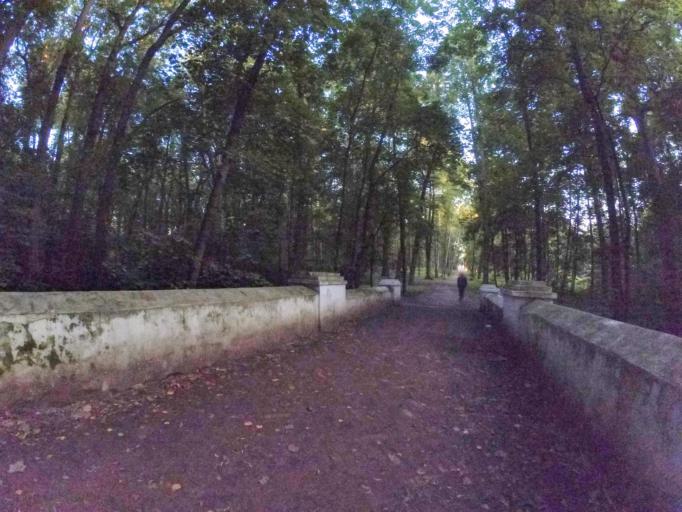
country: RU
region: Moscow
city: Strogino
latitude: 55.8505
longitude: 37.3983
